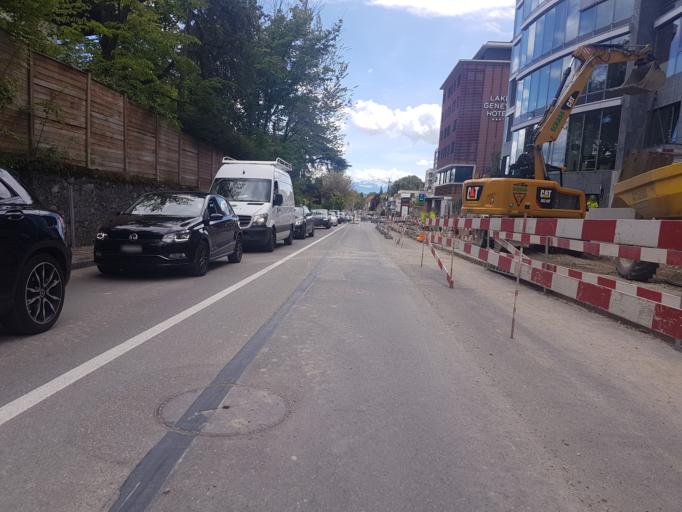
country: CH
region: Geneva
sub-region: Geneva
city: Versoix
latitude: 46.2818
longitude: 6.1662
